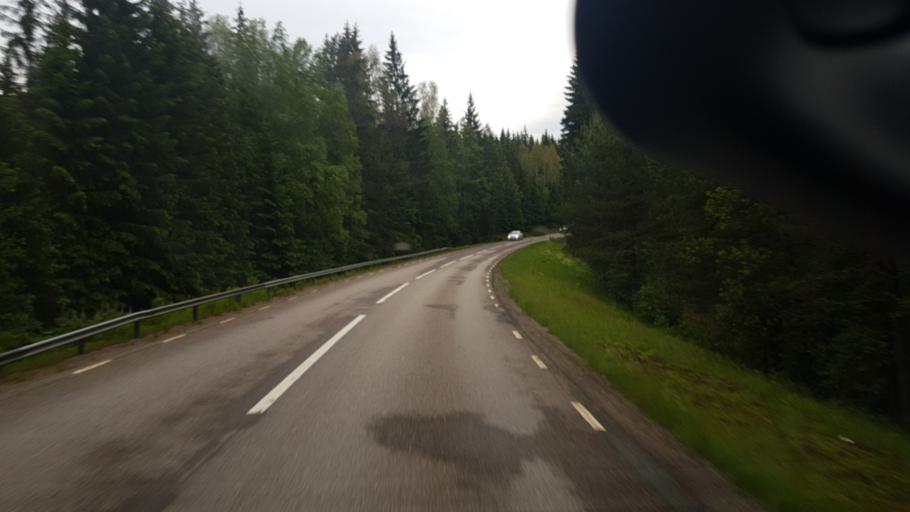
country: SE
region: Vaermland
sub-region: Eda Kommun
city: Amotfors
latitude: 59.6612
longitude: 12.3780
